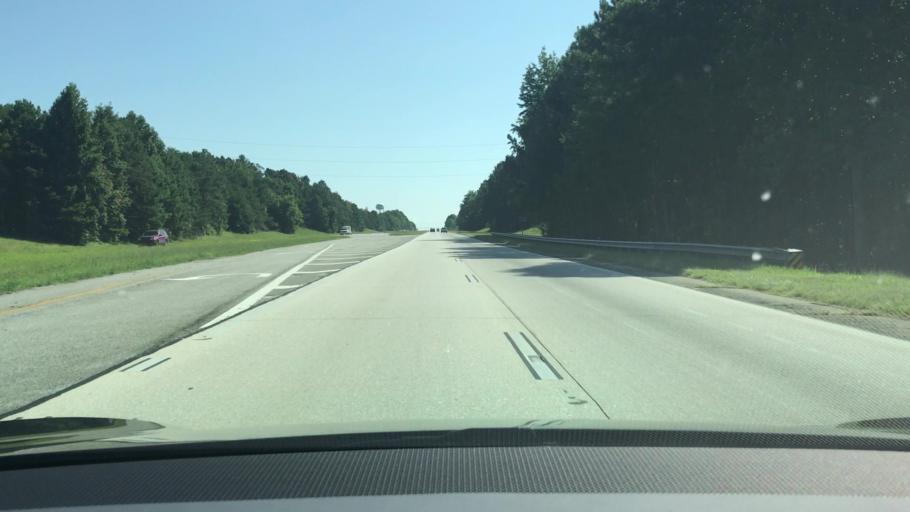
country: US
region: Georgia
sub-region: Hall County
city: Lula
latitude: 34.3881
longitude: -83.7029
